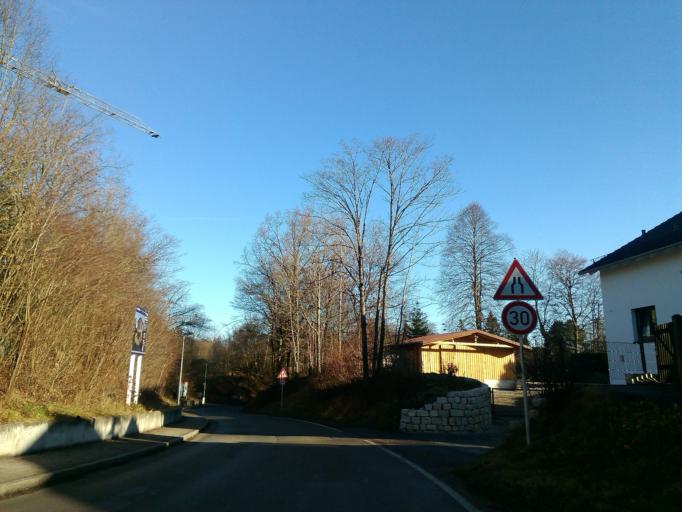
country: DE
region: Bavaria
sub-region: Upper Bavaria
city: Gauting
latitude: 48.0565
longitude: 11.3633
